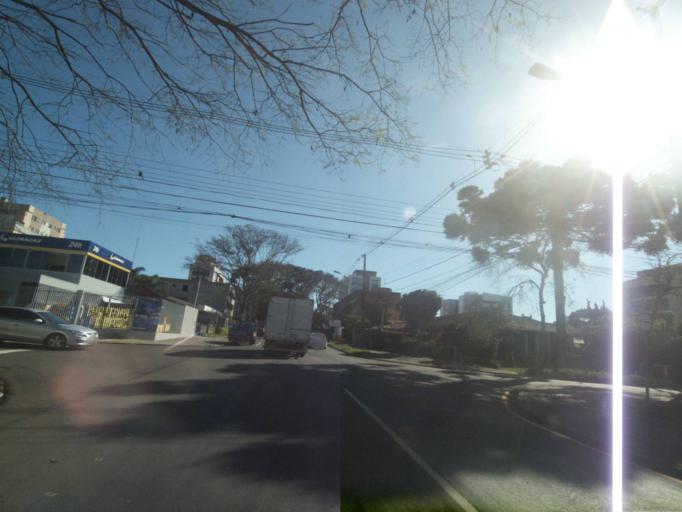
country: BR
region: Parana
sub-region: Curitiba
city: Curitiba
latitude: -25.3991
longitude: -49.2385
